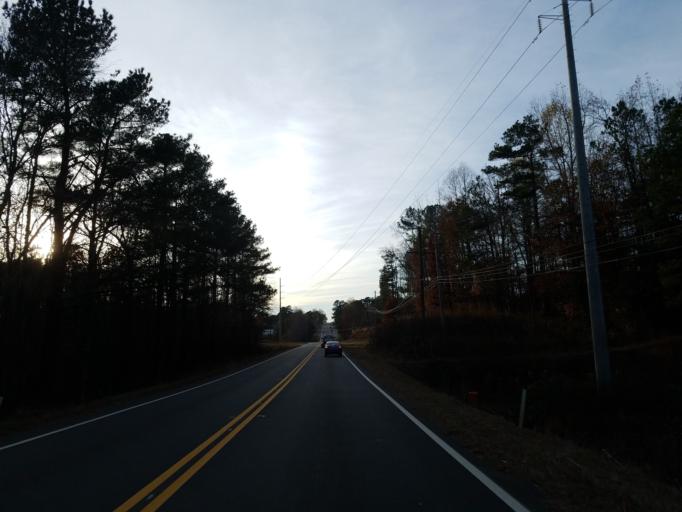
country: US
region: Georgia
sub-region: Haralson County
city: Bremen
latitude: 33.7220
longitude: -85.1053
